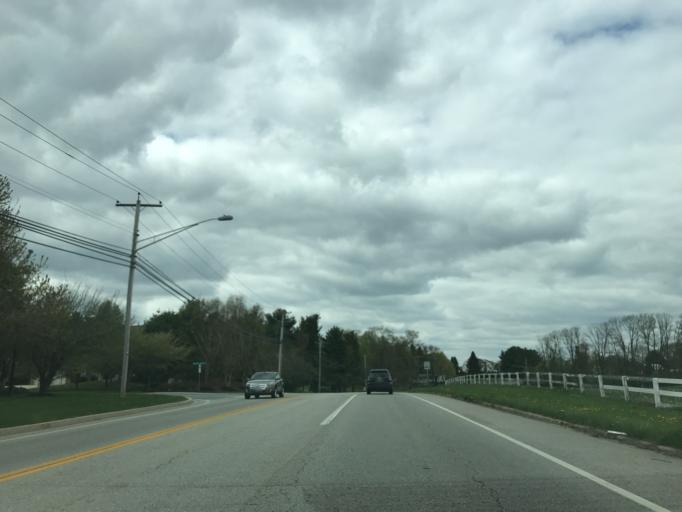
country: US
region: Maryland
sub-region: Harford County
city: Bel Air South
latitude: 39.5306
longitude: -76.2948
